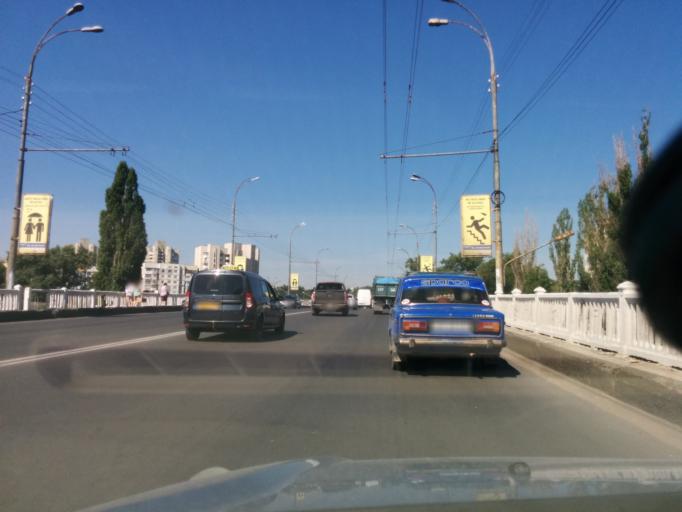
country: MD
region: Chisinau
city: Chisinau
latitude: 47.0223
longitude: 28.8582
